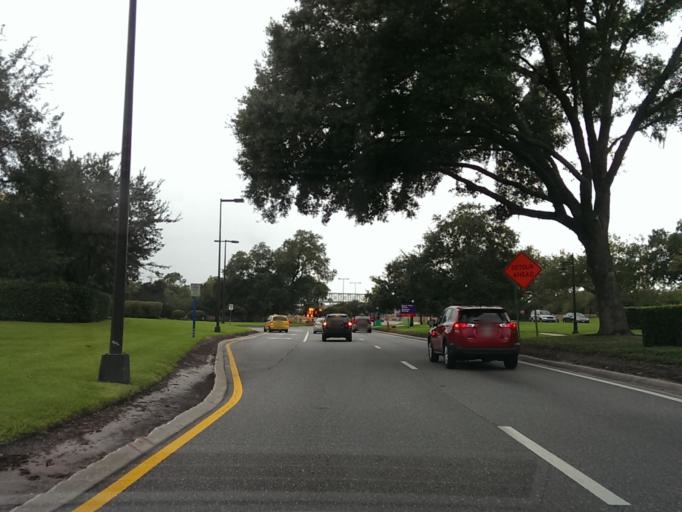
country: US
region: Florida
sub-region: Osceola County
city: Celebration
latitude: 28.3746
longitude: -81.5108
